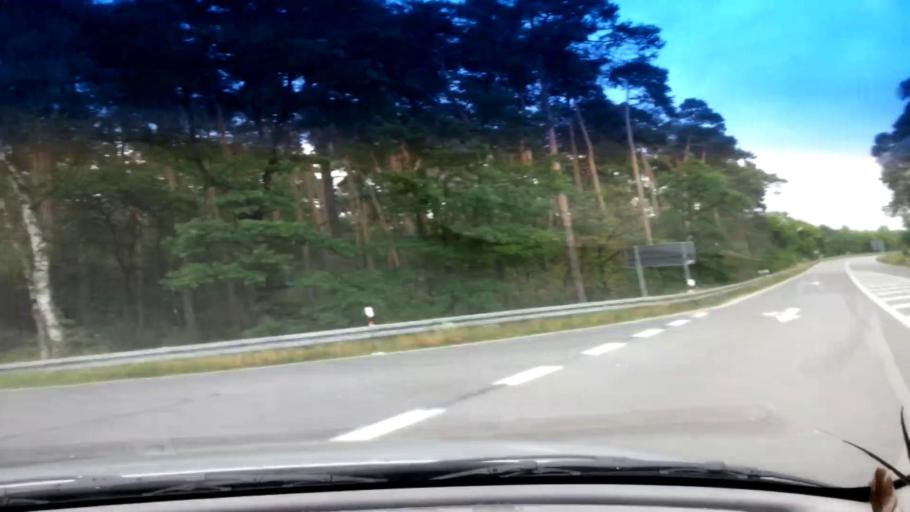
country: DE
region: Bavaria
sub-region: Upper Franconia
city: Hirschaid
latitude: 49.8298
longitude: 10.9807
